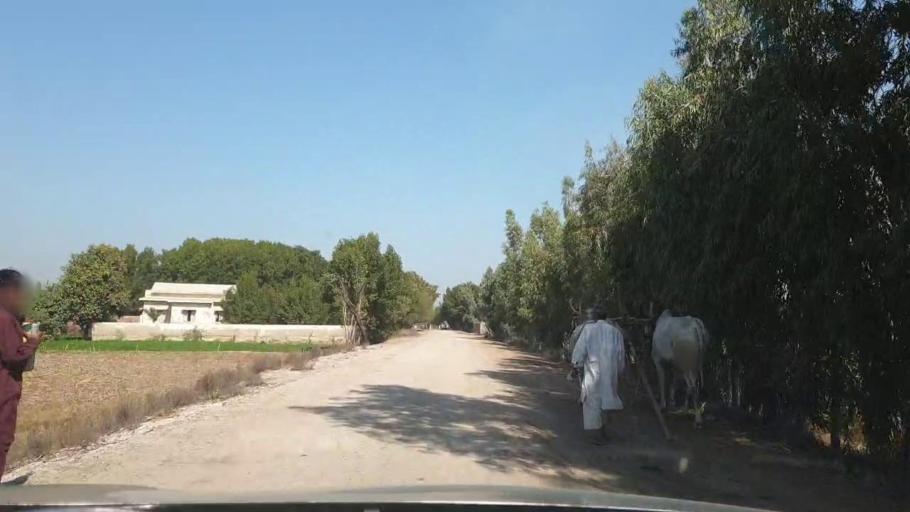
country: PK
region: Sindh
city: Tando Adam
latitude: 25.6101
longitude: 68.6437
